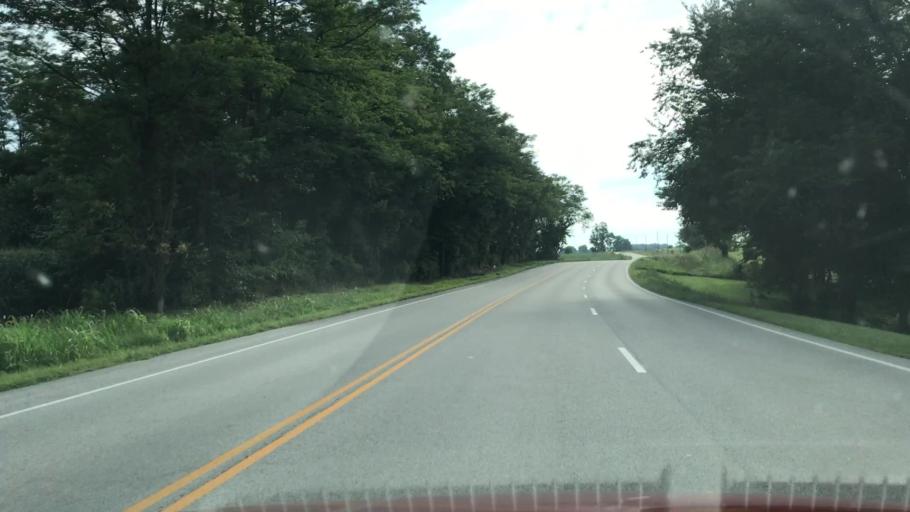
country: US
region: Kentucky
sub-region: Edmonson County
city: Brownsville
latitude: 37.0728
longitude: -86.2624
